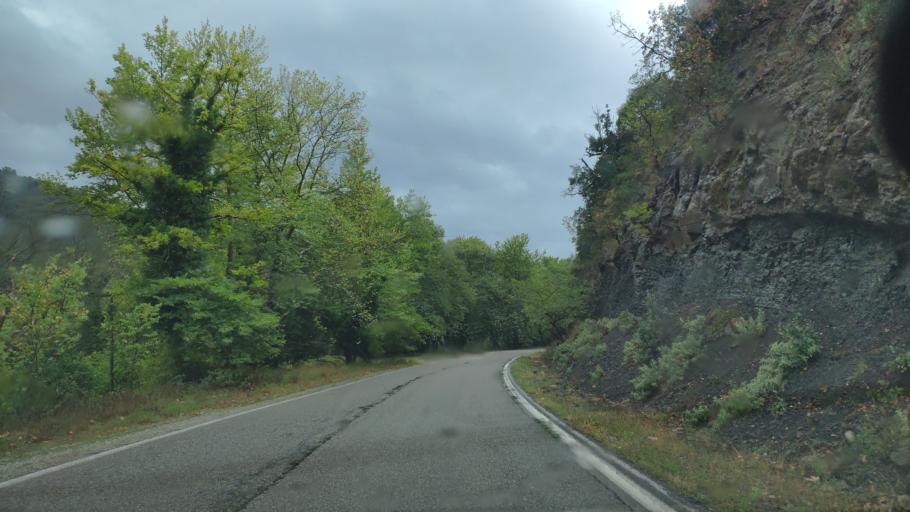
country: GR
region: West Greece
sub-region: Nomos Aitolias kai Akarnanias
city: Krikellos
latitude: 38.9582
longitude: 21.3374
